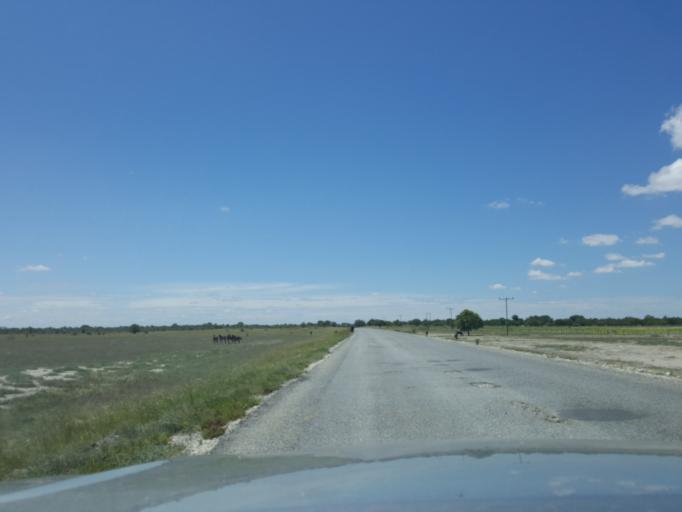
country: BW
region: Central
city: Nata
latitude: -20.1587
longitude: 25.8444
